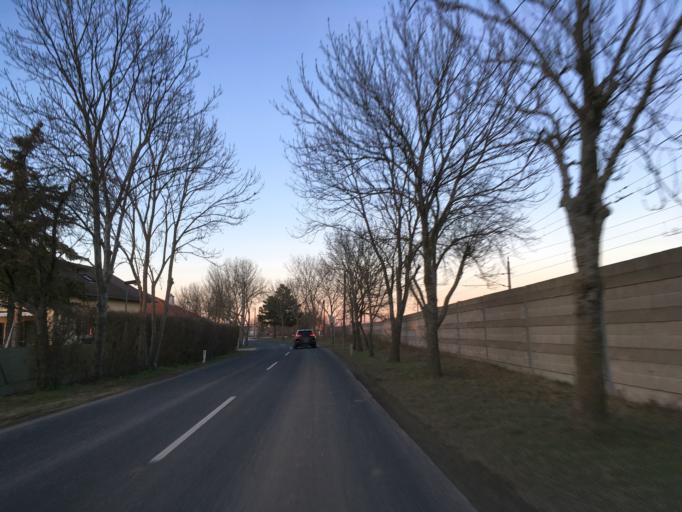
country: AT
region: Lower Austria
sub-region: Politischer Bezirk Baden
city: Ebreichsdorf
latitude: 47.9532
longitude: 16.4283
